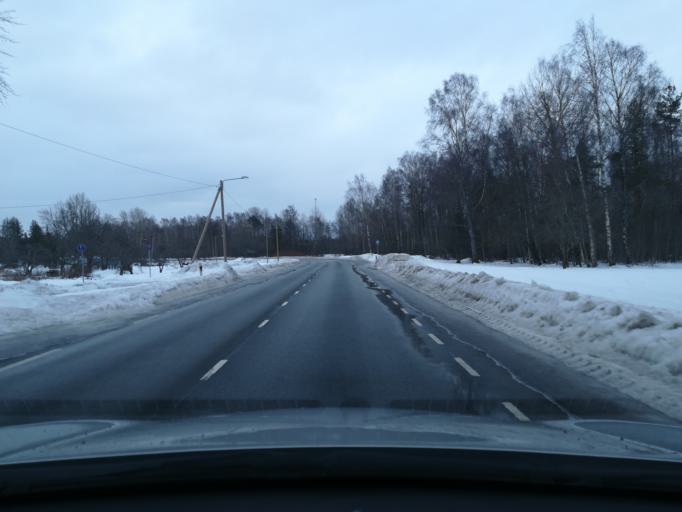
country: EE
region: Harju
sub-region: Nissi vald
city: Turba
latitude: 59.0751
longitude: 24.2403
